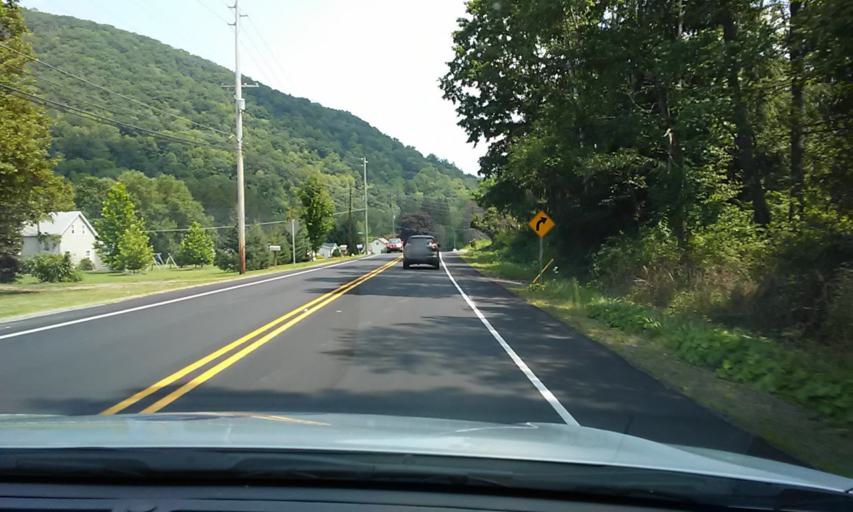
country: US
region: Pennsylvania
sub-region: Cameron County
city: Emporium
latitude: 41.4771
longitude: -78.3676
